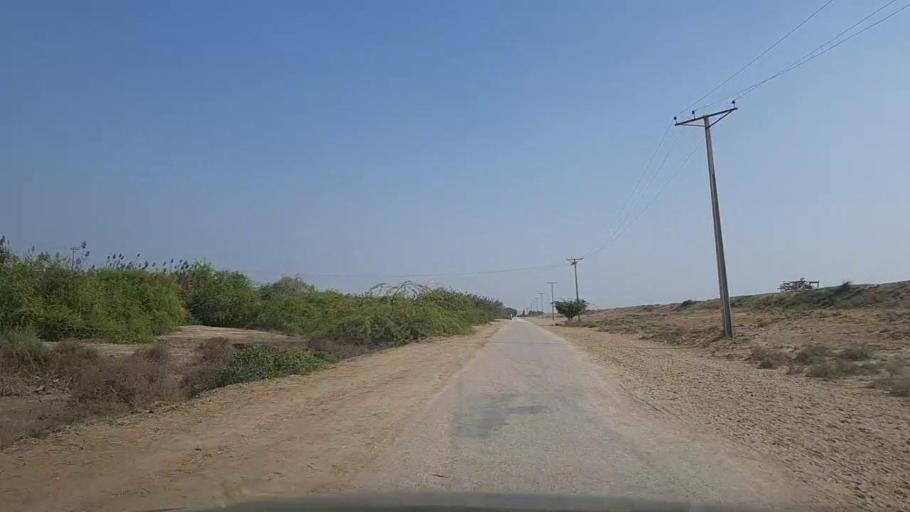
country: PK
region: Sindh
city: Thatta
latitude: 24.5835
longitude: 67.9188
